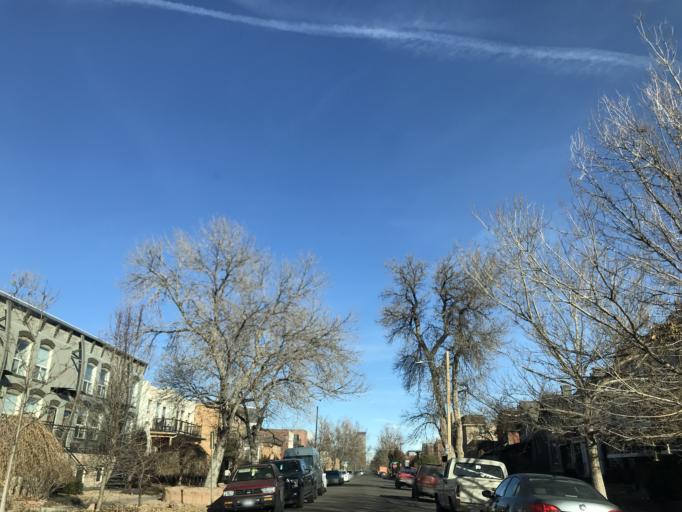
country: US
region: Colorado
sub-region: Denver County
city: Denver
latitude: 39.7154
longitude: -104.9851
